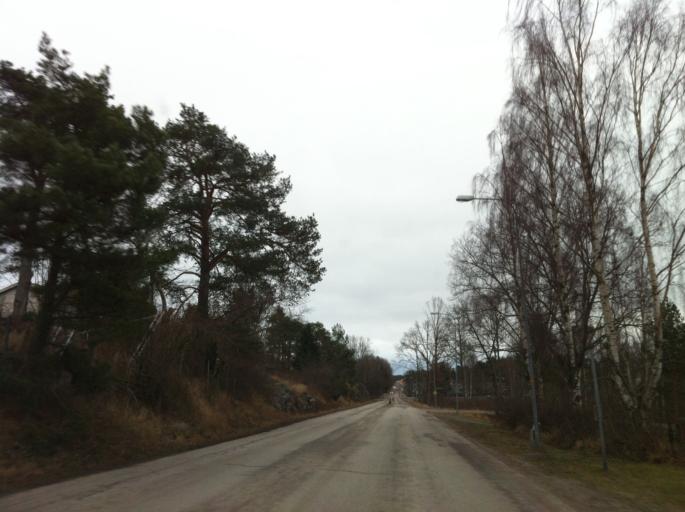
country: SE
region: Kalmar
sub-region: Vasterviks Kommun
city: Vaestervik
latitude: 57.8053
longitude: 16.5972
